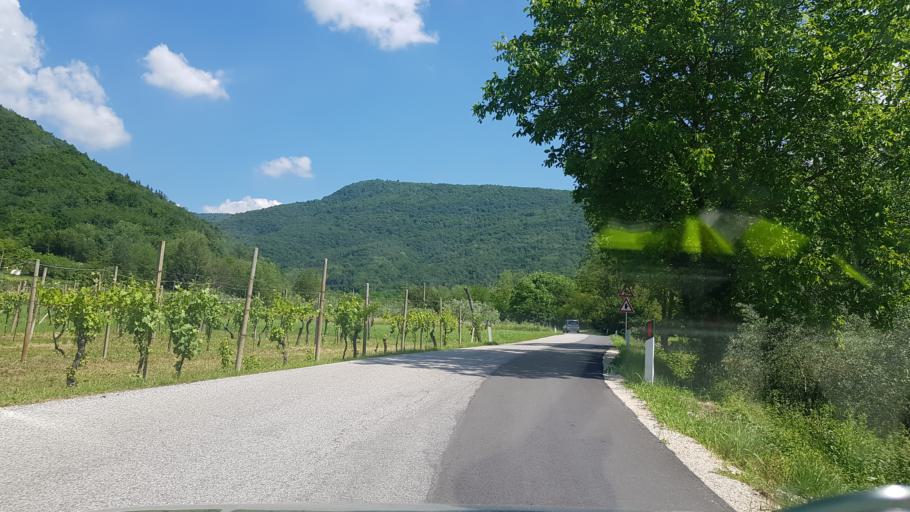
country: IT
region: Friuli Venezia Giulia
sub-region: Provincia di Udine
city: Torreano
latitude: 46.1364
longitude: 13.4381
